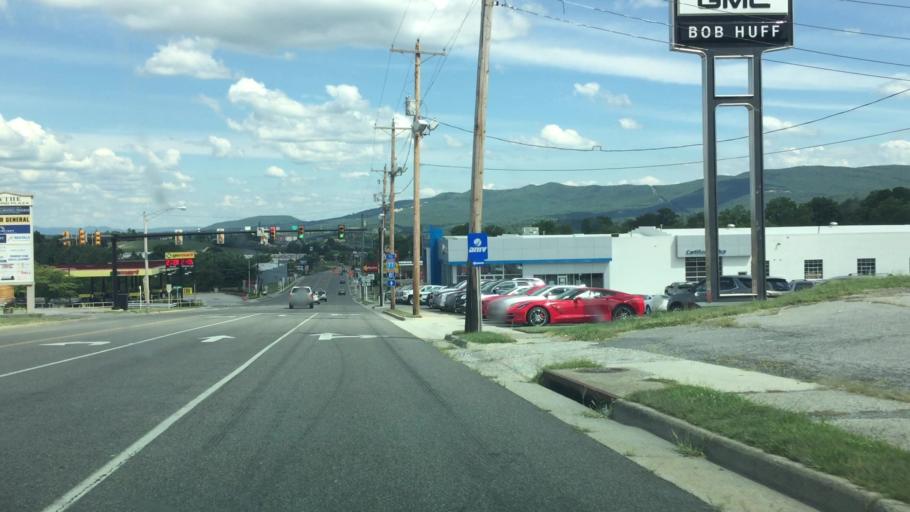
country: US
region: Virginia
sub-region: Wythe County
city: Wytheville
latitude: 36.9532
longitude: -81.0755
